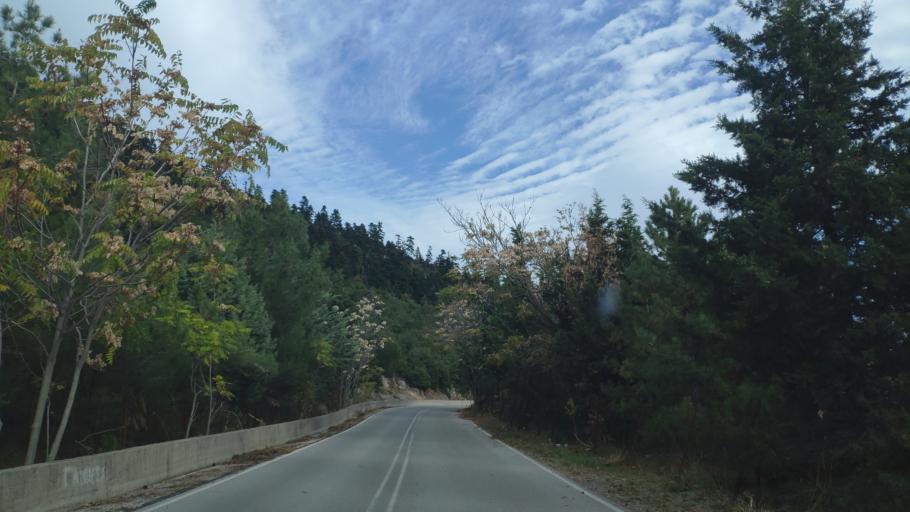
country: GR
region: Central Greece
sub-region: Nomos Fokidos
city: Amfissa
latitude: 38.6357
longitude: 22.3805
